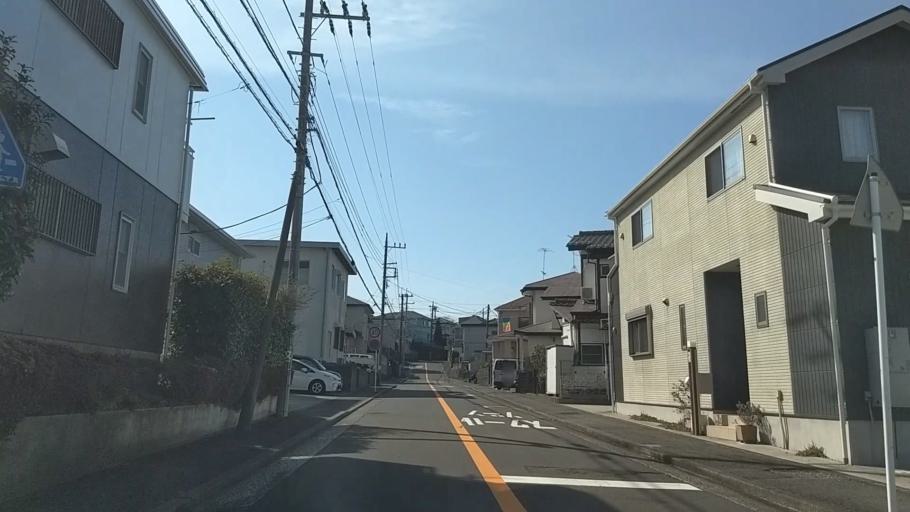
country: JP
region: Kanagawa
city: Kamakura
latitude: 35.3911
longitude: 139.5557
